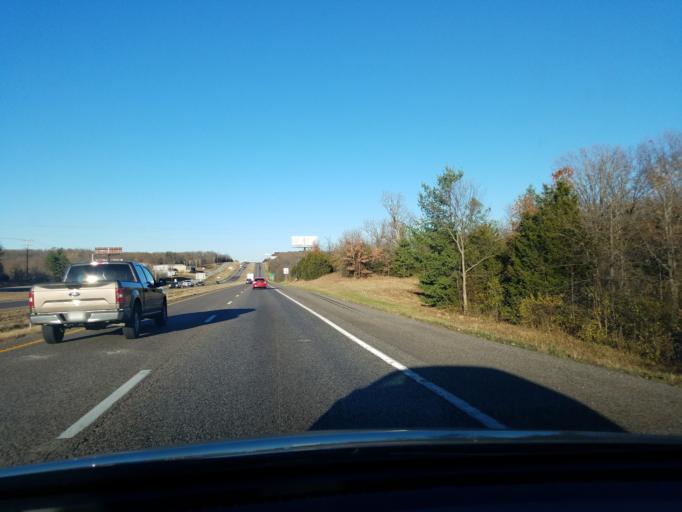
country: US
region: Missouri
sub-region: Franklin County
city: Sullivan
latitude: 38.2300
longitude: -91.1504
